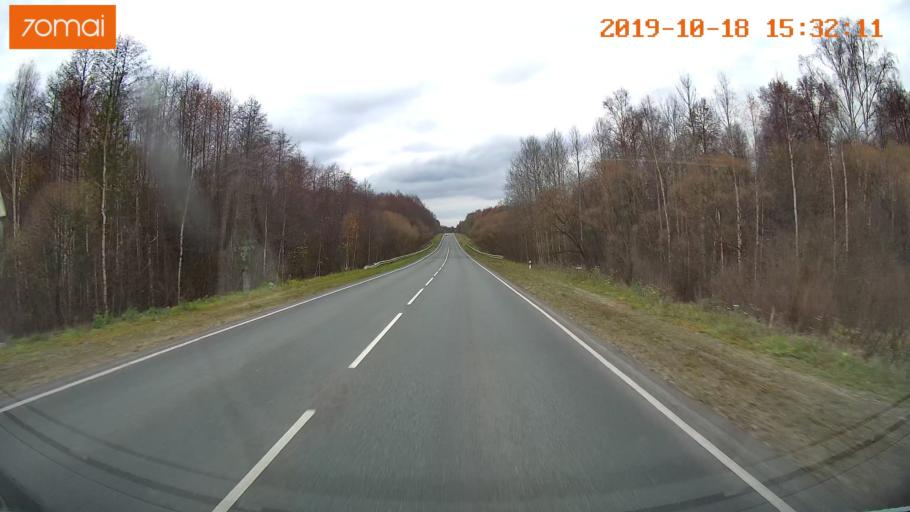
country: RU
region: Vladimir
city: Anopino
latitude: 55.8227
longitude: 40.6579
